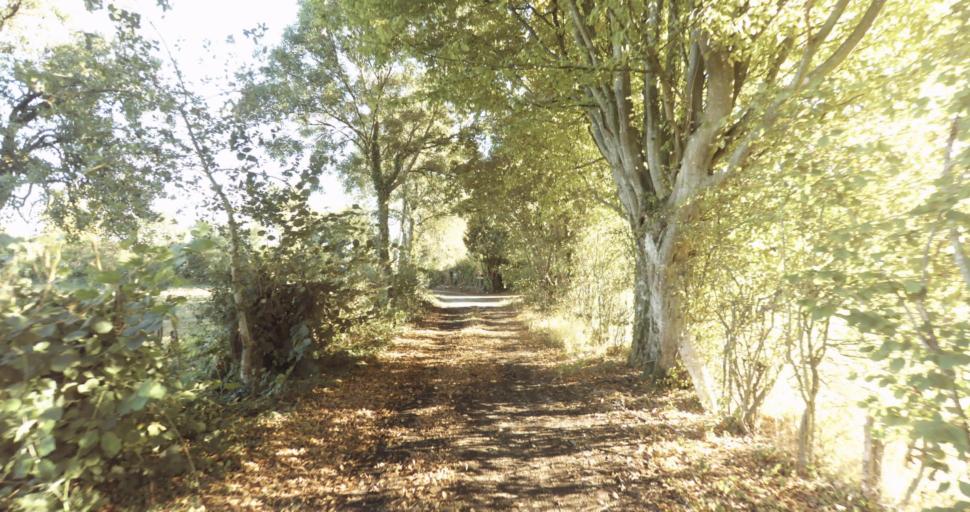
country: FR
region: Lower Normandy
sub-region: Departement de l'Orne
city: Vimoutiers
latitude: 48.8984
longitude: 0.1259
